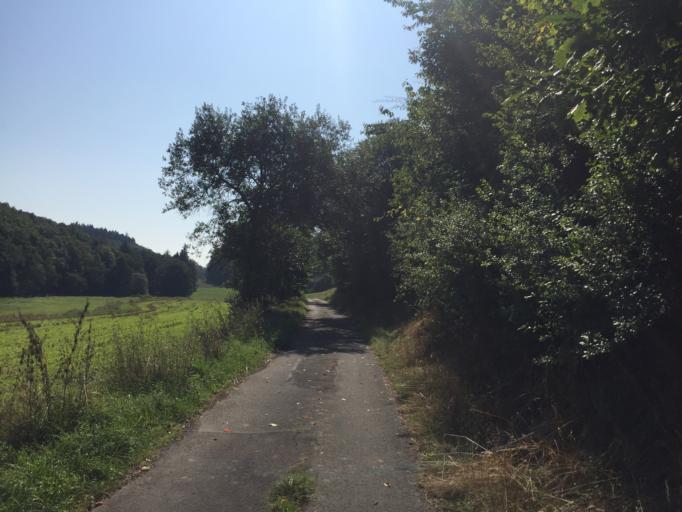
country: DE
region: Hesse
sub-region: Regierungsbezirk Giessen
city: Hoernsheim
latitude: 50.4434
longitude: 8.5742
